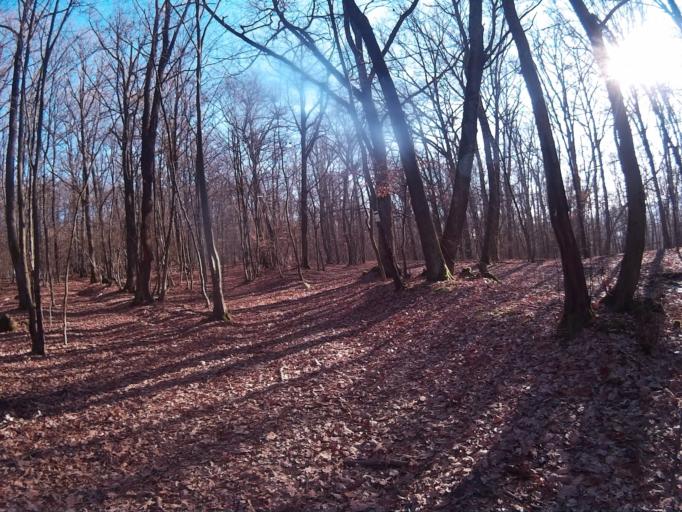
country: HU
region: Borsod-Abauj-Zemplen
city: Rudabanya
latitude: 48.4895
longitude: 20.5755
